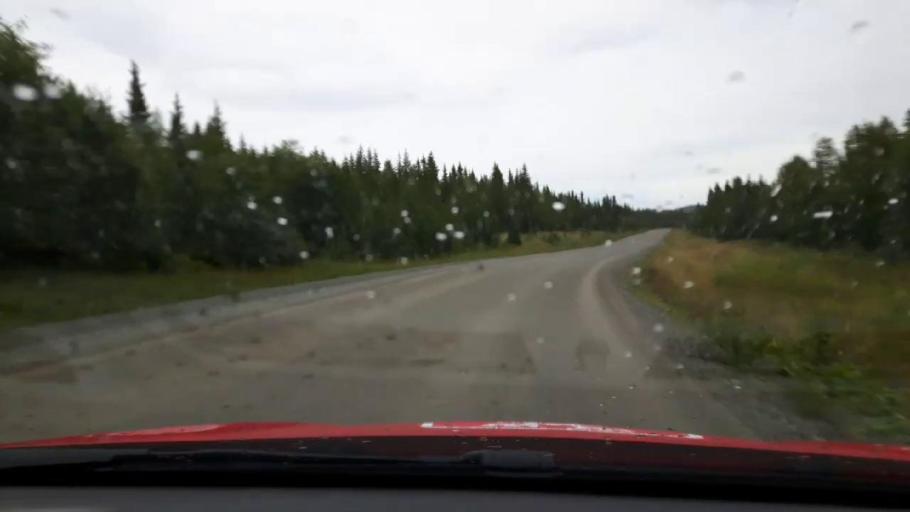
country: SE
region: Jaemtland
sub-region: Are Kommun
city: Are
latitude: 63.4502
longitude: 12.6753
